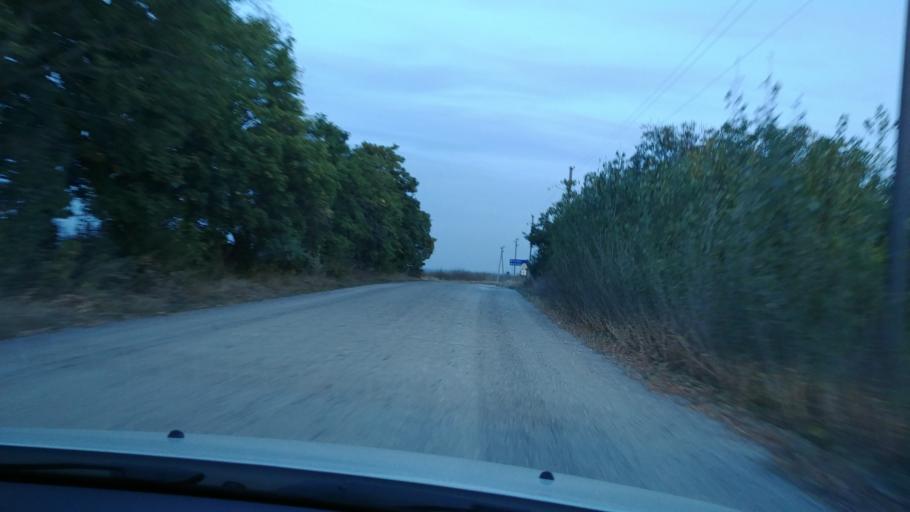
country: MD
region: Rezina
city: Saharna
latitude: 47.6696
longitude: 28.9433
